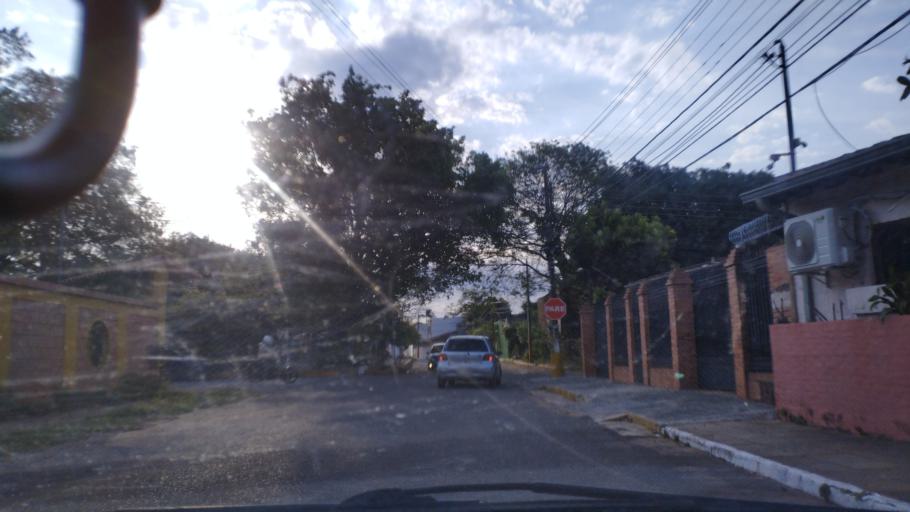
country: PY
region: Central
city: Fernando de la Mora
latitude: -25.3117
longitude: -57.5367
